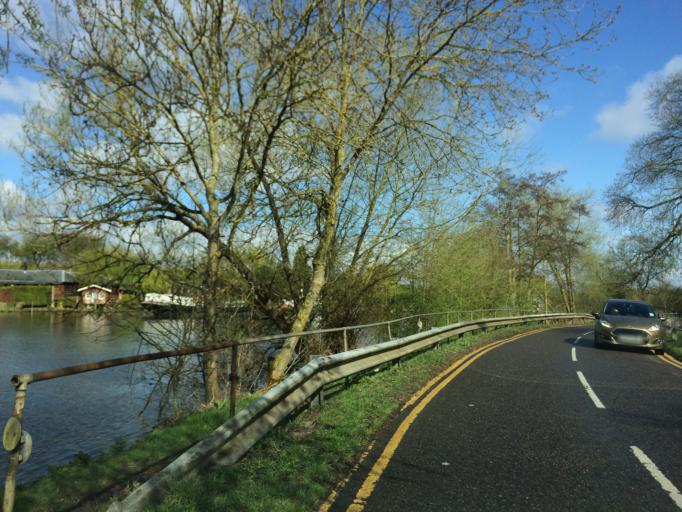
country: GB
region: England
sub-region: Surrey
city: Chertsey
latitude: 51.4002
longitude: -0.4913
